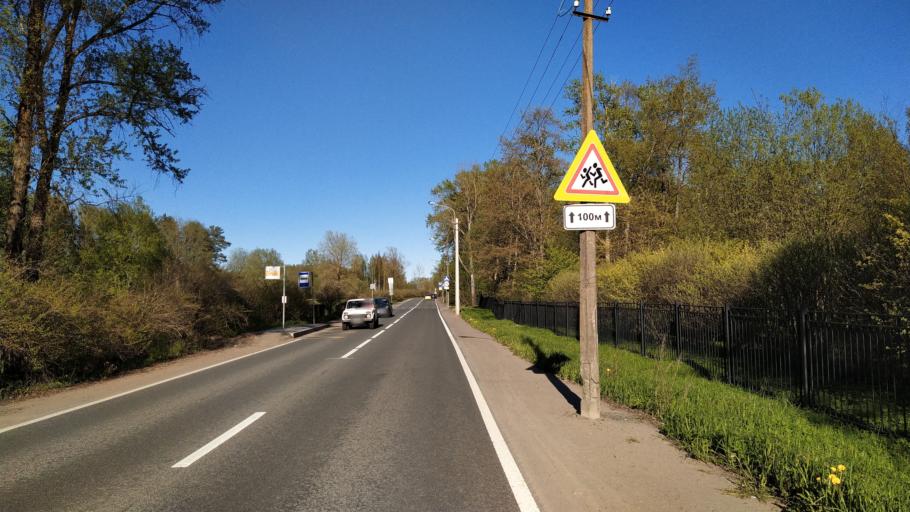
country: RU
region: St.-Petersburg
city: Tyarlevo
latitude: 59.6853
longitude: 30.4758
